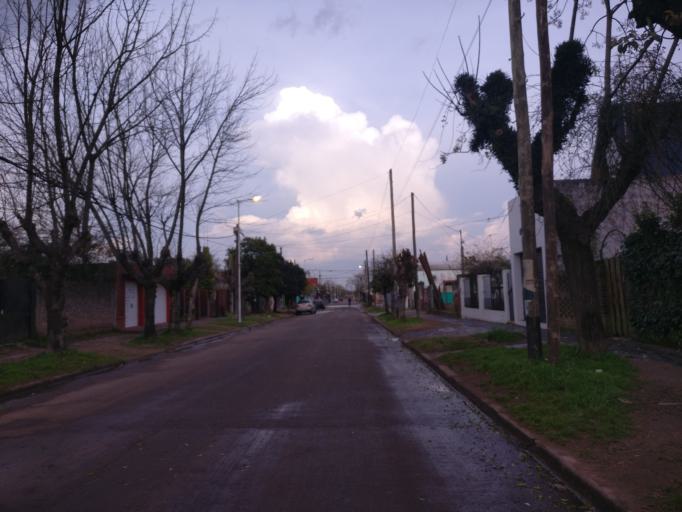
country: AR
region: Buenos Aires
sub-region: Partido de Ezeiza
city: Ezeiza
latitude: -34.9406
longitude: -58.6153
